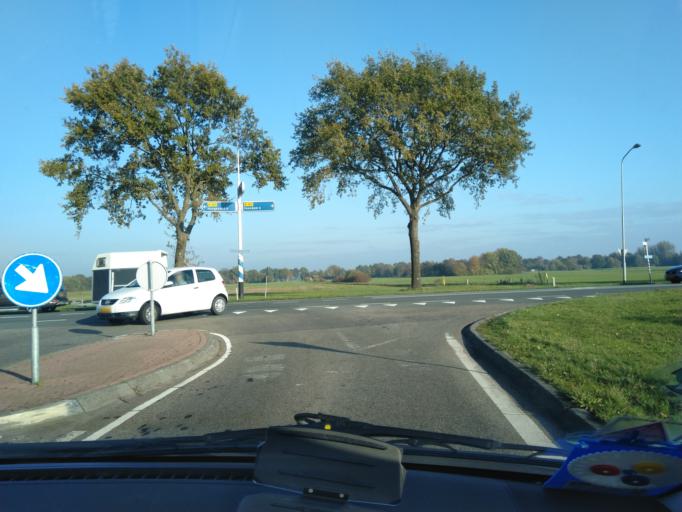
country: NL
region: Groningen
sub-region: Gemeente Hoogezand-Sappemeer
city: Sappemeer
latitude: 53.1256
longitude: 6.7801
